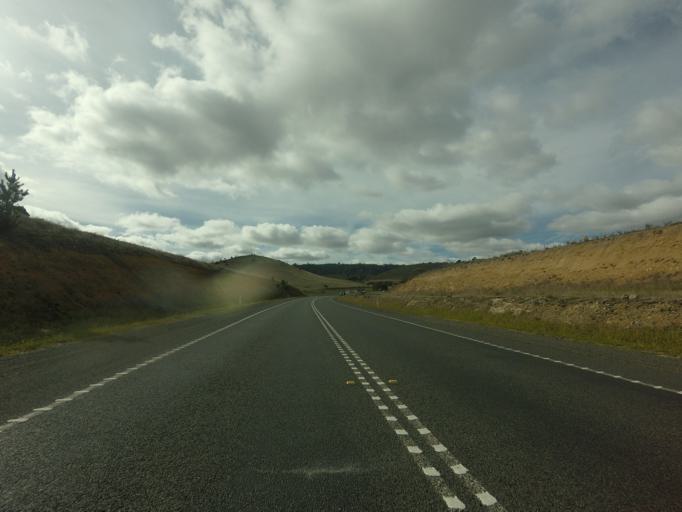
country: AU
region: Tasmania
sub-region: Brighton
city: Bridgewater
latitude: -42.4426
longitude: 147.2286
